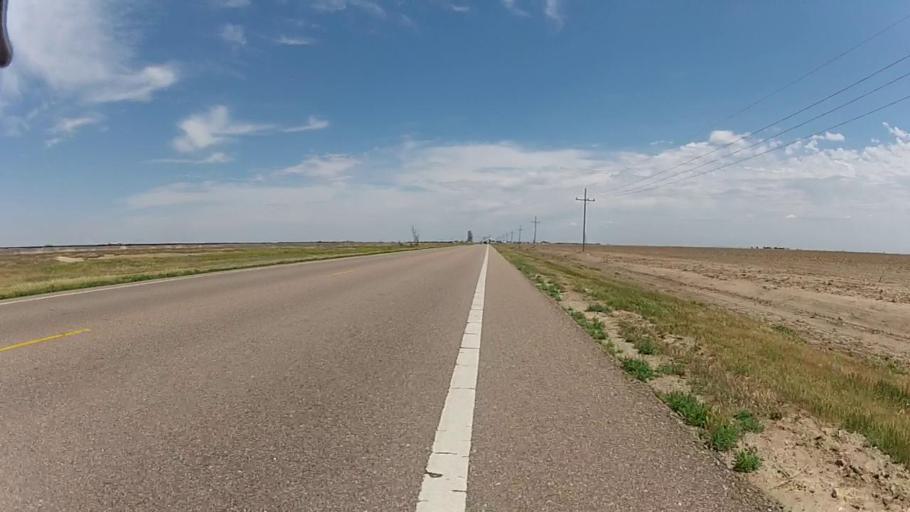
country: US
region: Kansas
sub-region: Haskell County
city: Sublette
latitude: 37.4710
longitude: -100.8882
